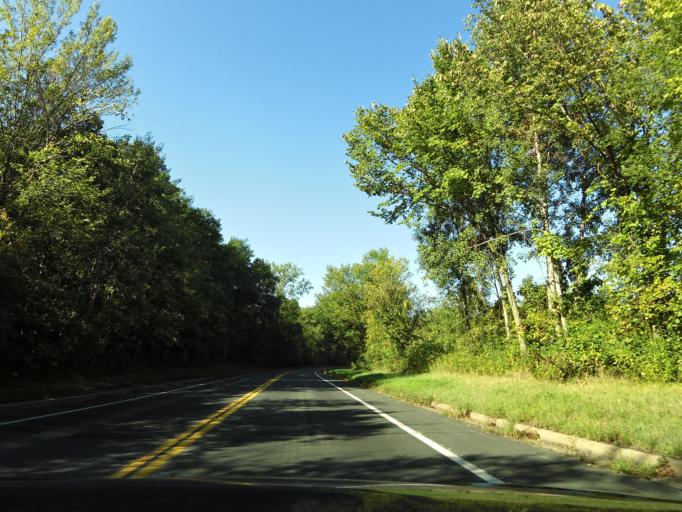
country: US
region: Minnesota
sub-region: Scott County
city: Savage
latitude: 44.7328
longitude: -93.3255
